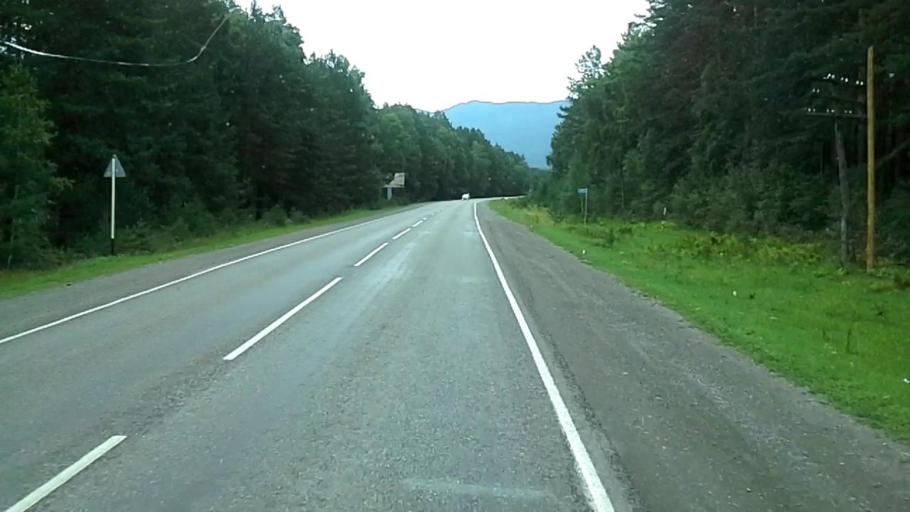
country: RU
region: Altay
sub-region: Mayminskiy Rayon
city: Manzherok
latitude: 51.8337
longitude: 85.7464
